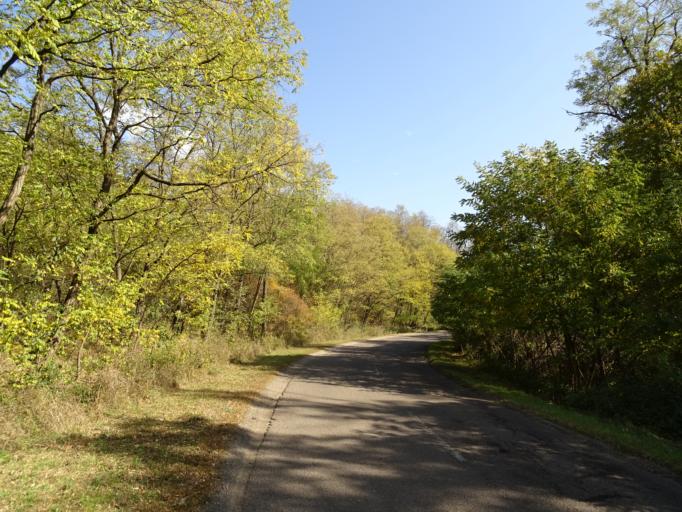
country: HU
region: Nograd
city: Salgotarjan
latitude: 48.0508
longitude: 19.7544
